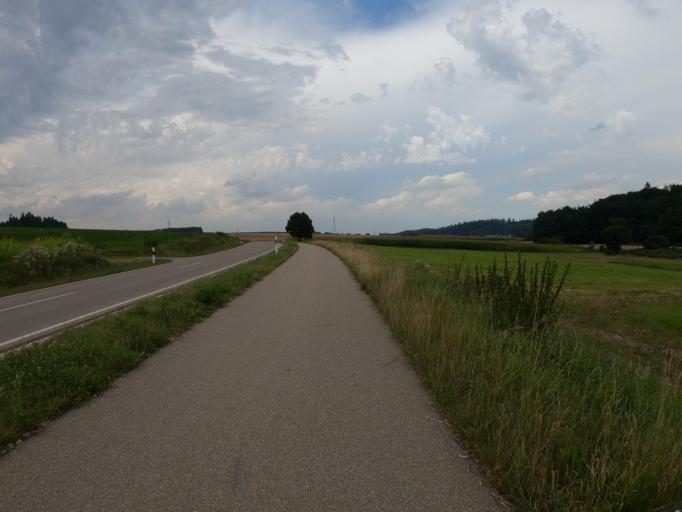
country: DE
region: Bavaria
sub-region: Swabia
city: Pfaffenhofen an der Roth
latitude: 48.3631
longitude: 10.2060
